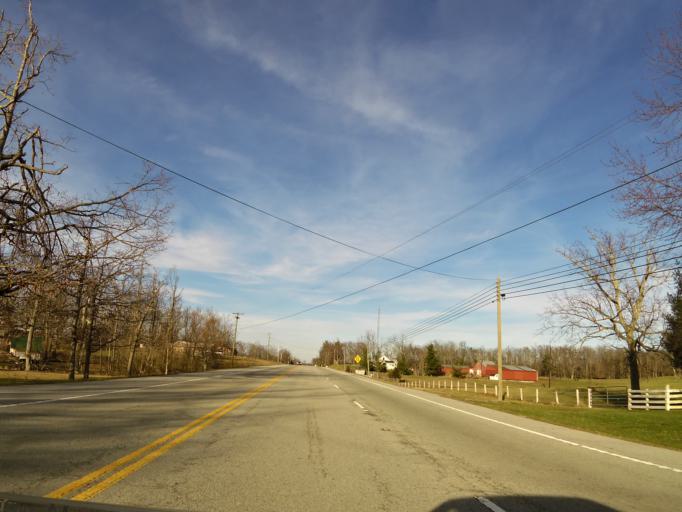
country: US
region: Tennessee
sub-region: White County
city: Sparta
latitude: 35.9326
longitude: -85.3784
